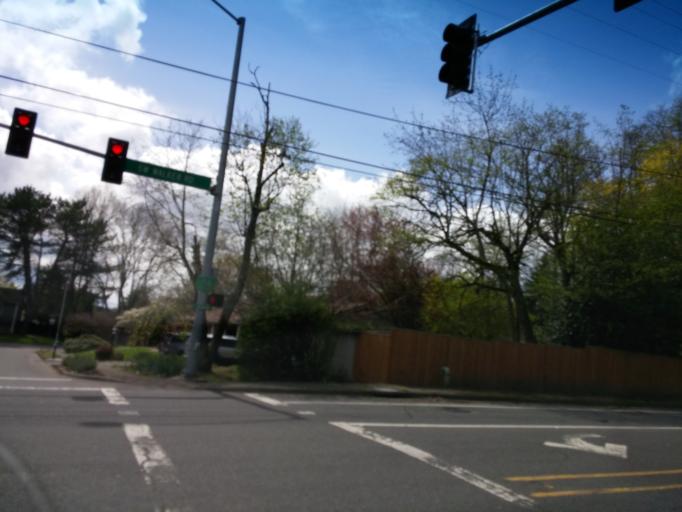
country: US
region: Oregon
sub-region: Washington County
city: Cedar Hills
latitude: 45.5000
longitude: -122.7958
